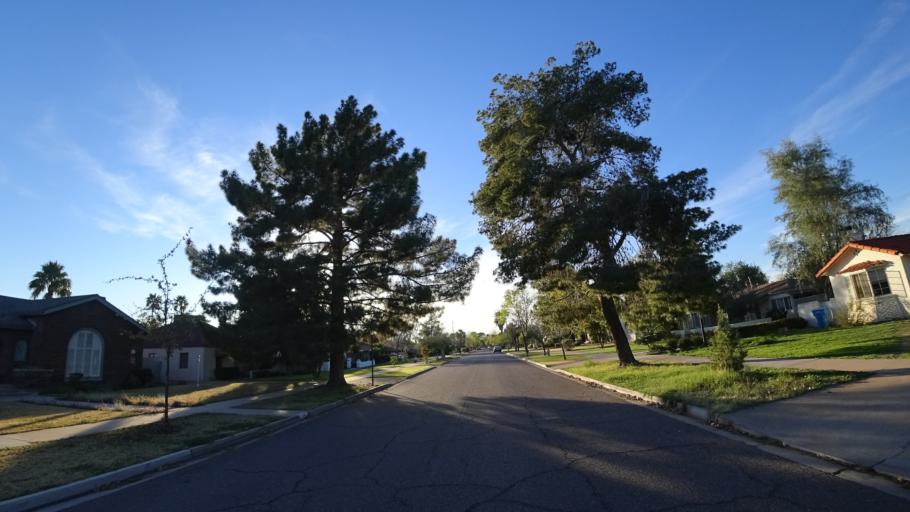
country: US
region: Arizona
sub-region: Maricopa County
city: Phoenix
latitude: 33.4759
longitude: -112.0922
